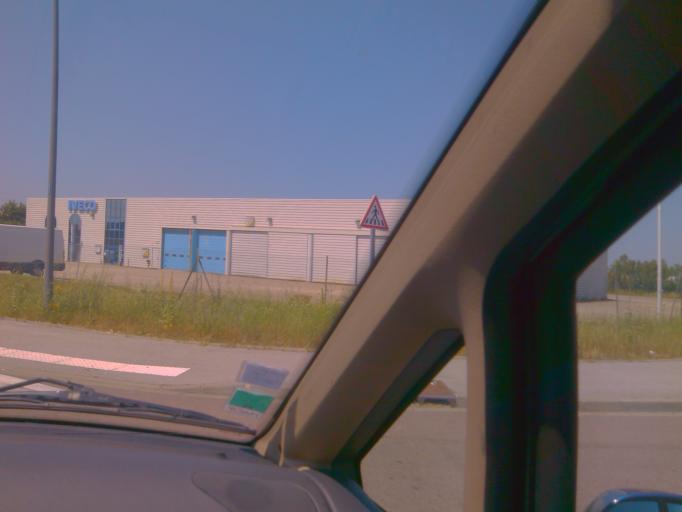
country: FR
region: Bourgogne
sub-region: Departement de Saone-et-Loire
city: Saint-Marcel
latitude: 46.7686
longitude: 4.8705
